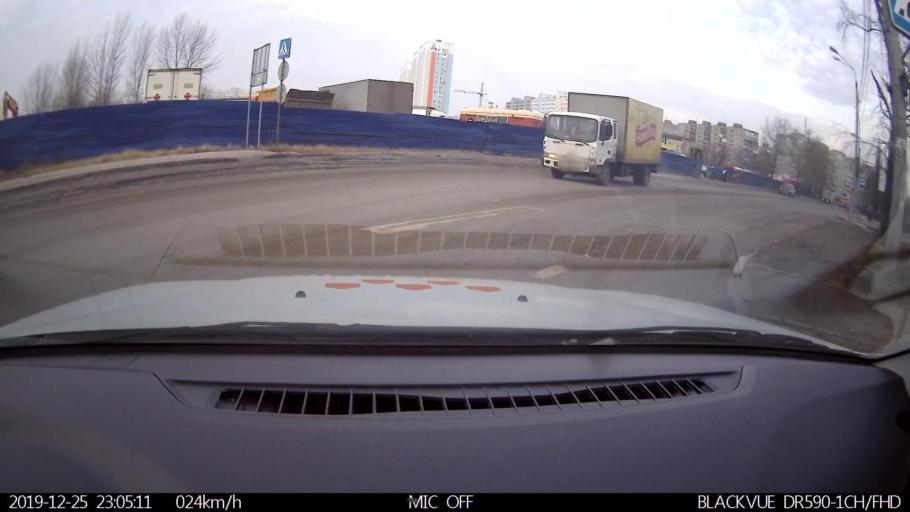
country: RU
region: Nizjnij Novgorod
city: Gorbatovka
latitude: 56.3592
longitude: 43.8055
